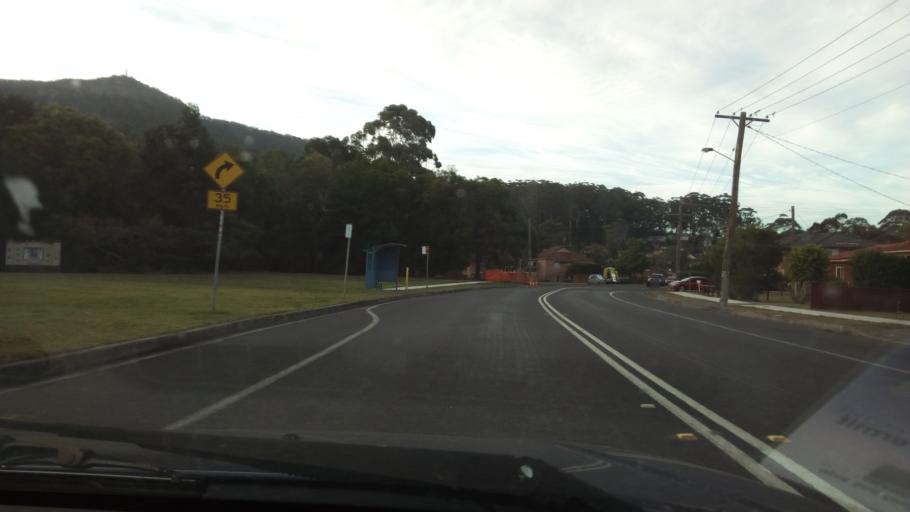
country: AU
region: New South Wales
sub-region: Wollongong
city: Mount Ousley
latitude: -34.3818
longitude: 150.8820
